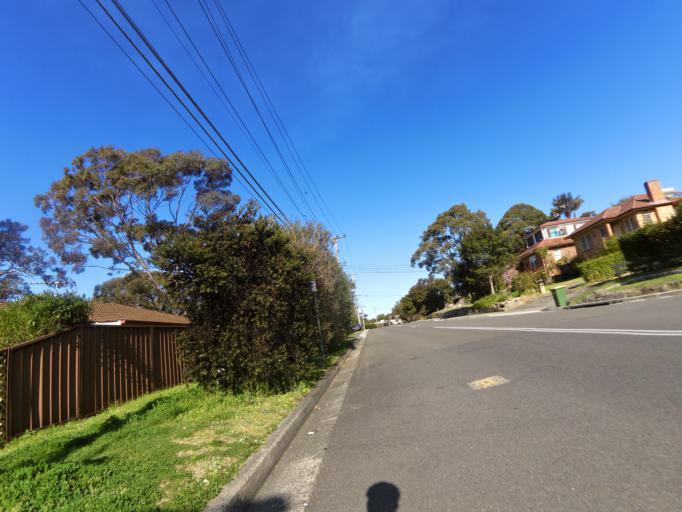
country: AU
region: New South Wales
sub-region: Sutherland Shire
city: Como
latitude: -34.0039
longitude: 151.0689
